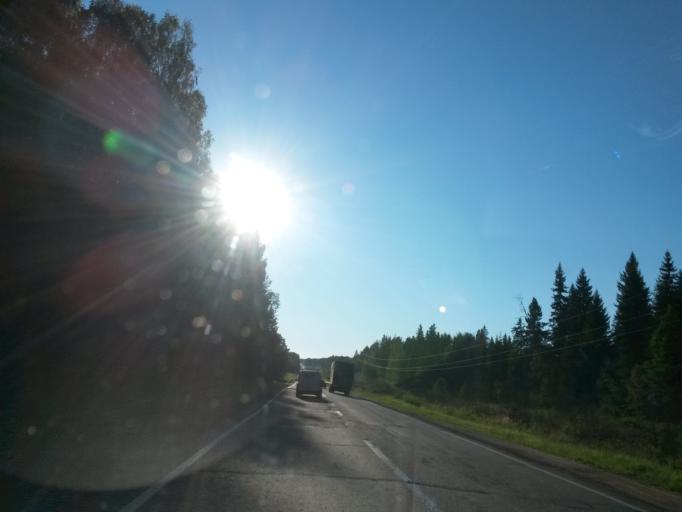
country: RU
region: Jaroslavl
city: Gavrilov-Yam
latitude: 57.2658
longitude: 40.0020
